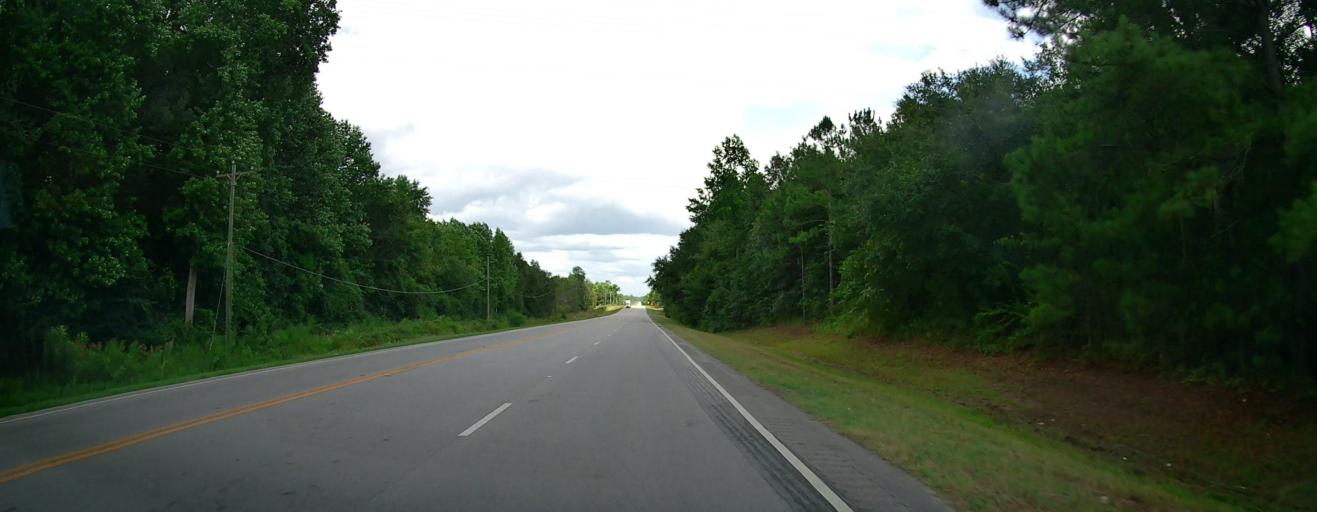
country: US
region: Georgia
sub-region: Coffee County
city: Broxton
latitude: 31.5664
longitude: -83.0067
